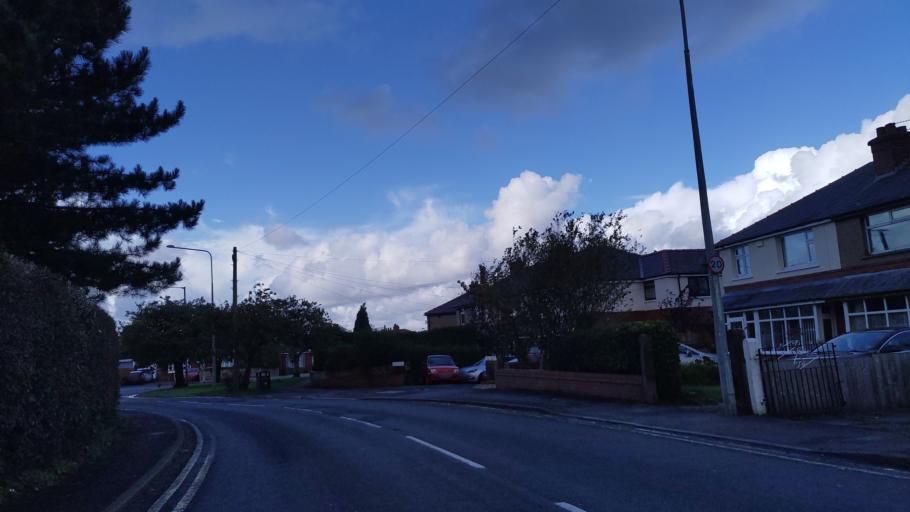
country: GB
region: England
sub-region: Lancashire
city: Chorley
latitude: 53.6402
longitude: -2.6297
